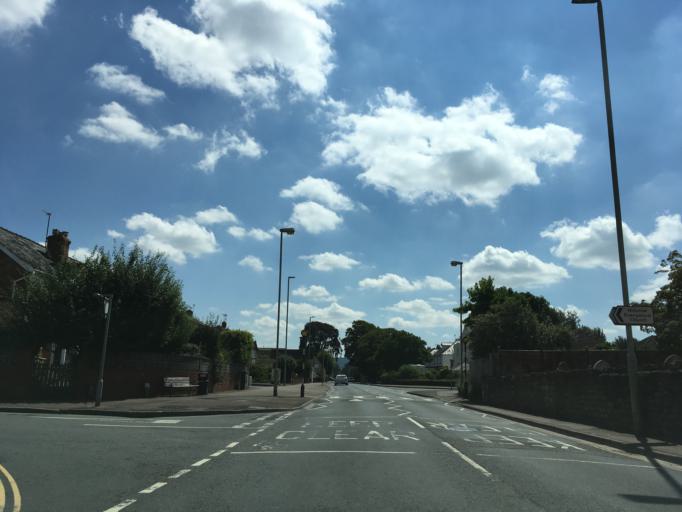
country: GB
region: England
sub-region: Gloucestershire
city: Barnwood
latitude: 51.8569
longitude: -2.1920
